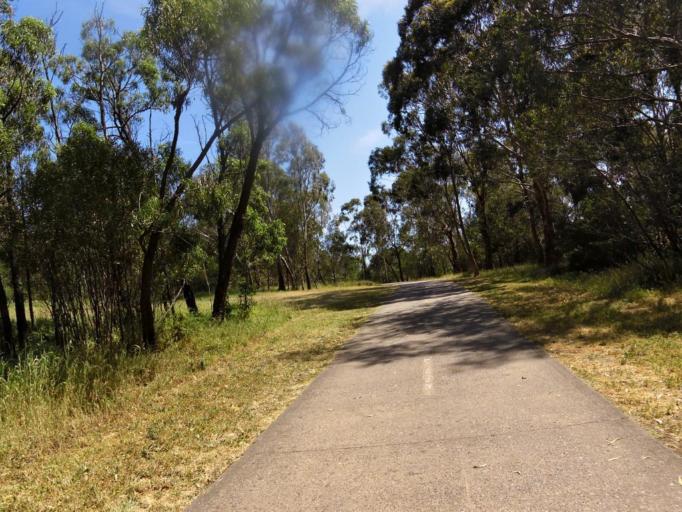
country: AU
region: Victoria
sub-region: Darebin
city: Fairfield
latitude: -37.7882
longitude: 145.0078
